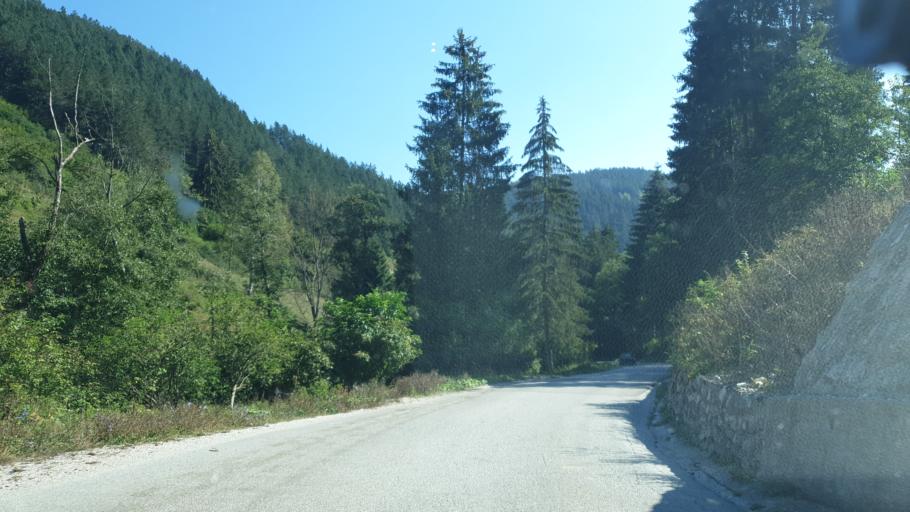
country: RS
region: Central Serbia
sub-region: Zlatiborski Okrug
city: Nova Varos
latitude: 43.4580
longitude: 19.8327
